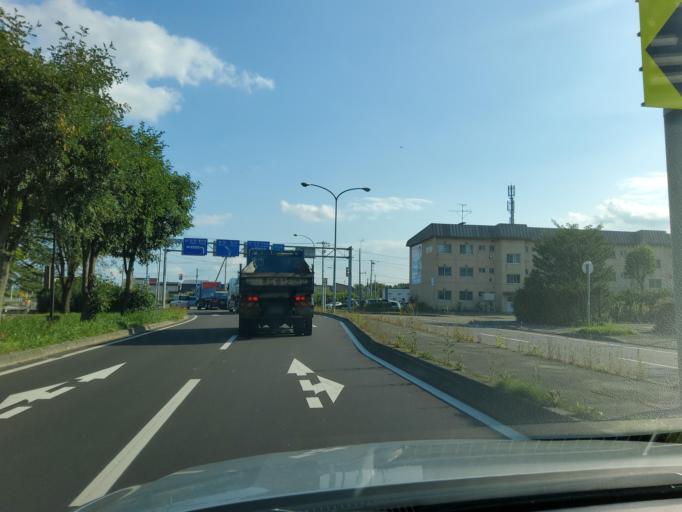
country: JP
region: Hokkaido
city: Obihiro
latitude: 42.9038
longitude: 143.2142
